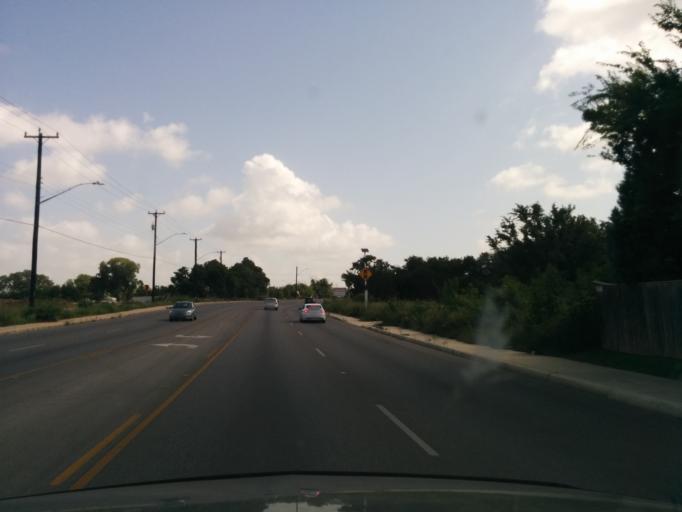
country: US
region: Texas
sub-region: Bexar County
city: Leon Valley
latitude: 29.5607
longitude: -98.6150
